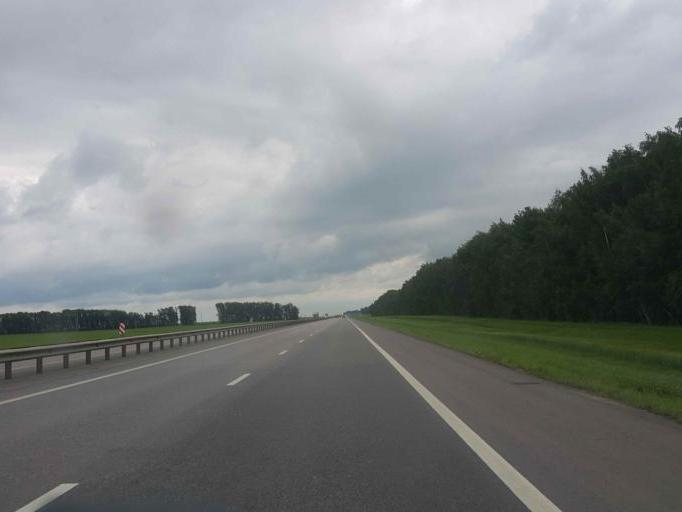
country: RU
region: Tambov
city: Zavoronezhskoye
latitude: 52.8339
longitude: 40.8734
